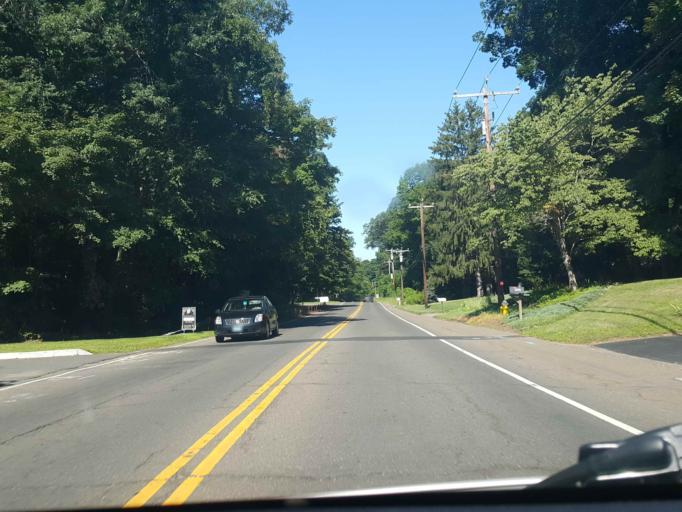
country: US
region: Connecticut
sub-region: New Haven County
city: North Branford
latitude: 41.3095
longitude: -72.7294
